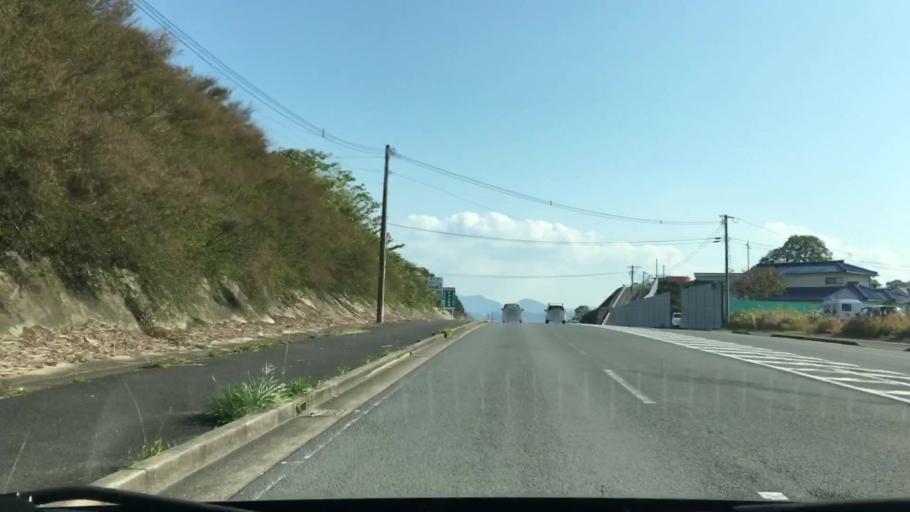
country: JP
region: Nagasaki
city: Togitsu
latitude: 32.8583
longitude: 129.8178
